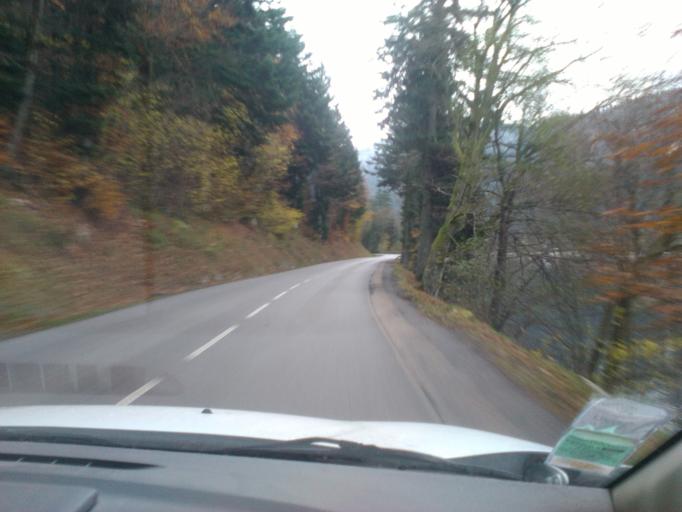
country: FR
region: Lorraine
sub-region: Departement des Vosges
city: Xonrupt-Longemer
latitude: 48.0700
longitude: 6.9554
